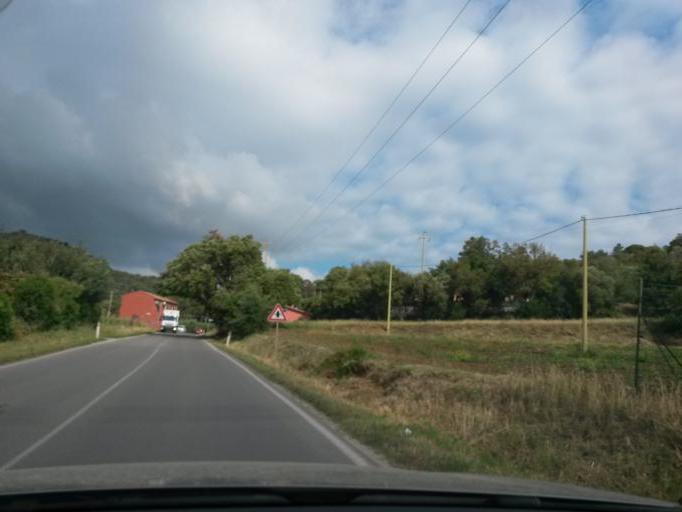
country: IT
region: Tuscany
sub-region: Provincia di Livorno
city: Capoliveri
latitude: 42.7785
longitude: 10.3486
